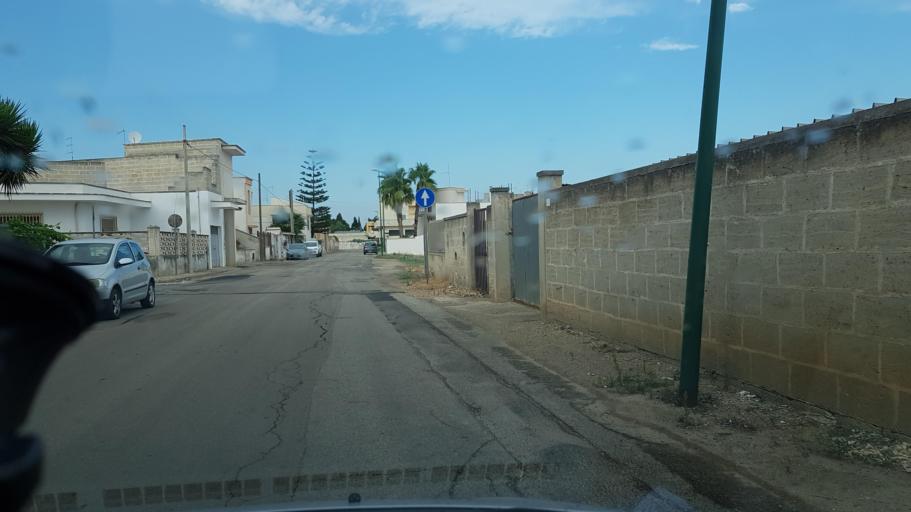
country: IT
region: Apulia
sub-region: Provincia di Brindisi
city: Torre Santa Susanna
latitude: 40.4614
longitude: 17.7459
